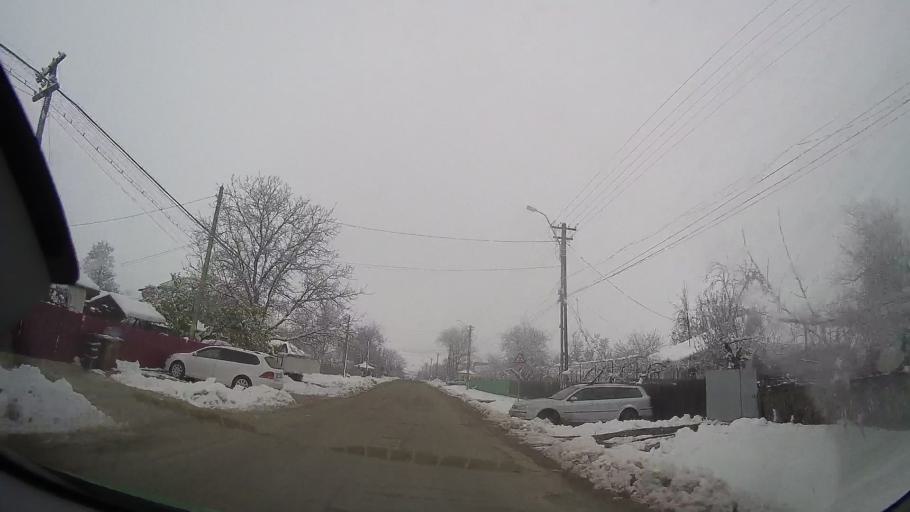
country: RO
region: Iasi
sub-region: Comuna Tibanesti
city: Tibanesti
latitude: 46.9044
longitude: 27.3334
